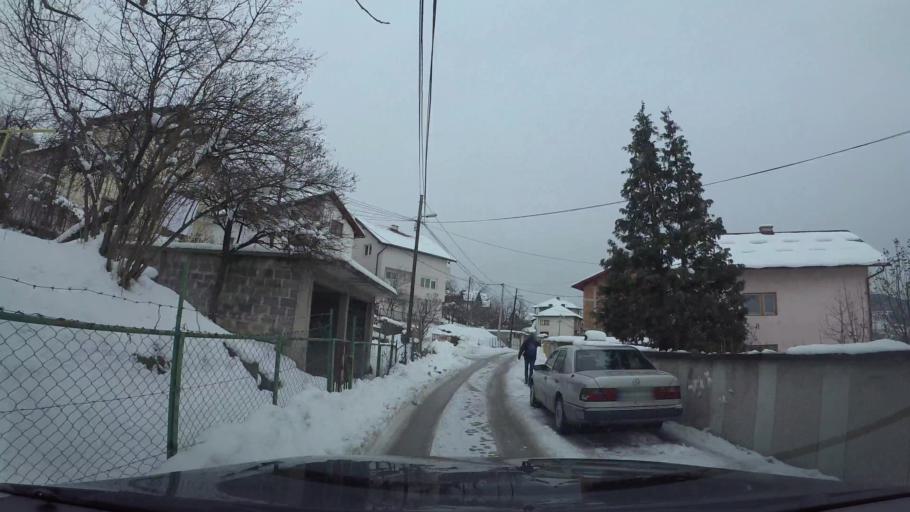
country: BA
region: Federation of Bosnia and Herzegovina
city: Kobilja Glava
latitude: 43.8637
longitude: 18.3911
